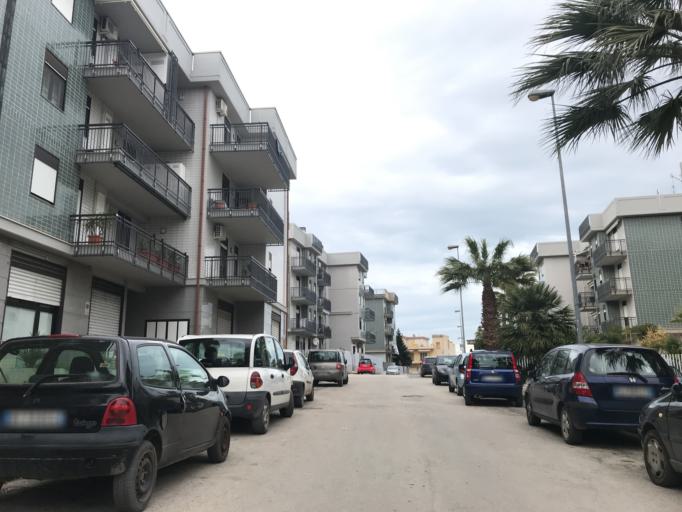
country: IT
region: Apulia
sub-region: Provincia di Bari
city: Corato
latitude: 41.1595
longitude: 16.4129
